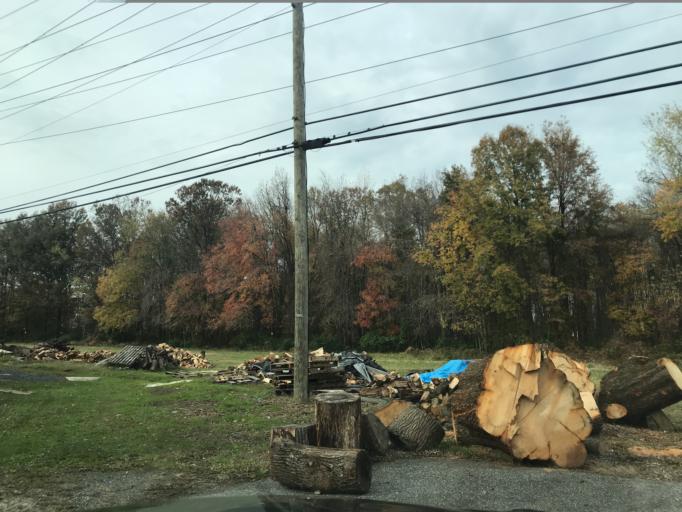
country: US
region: Maryland
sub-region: Baltimore County
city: Rossville
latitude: 39.3433
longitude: -76.4600
